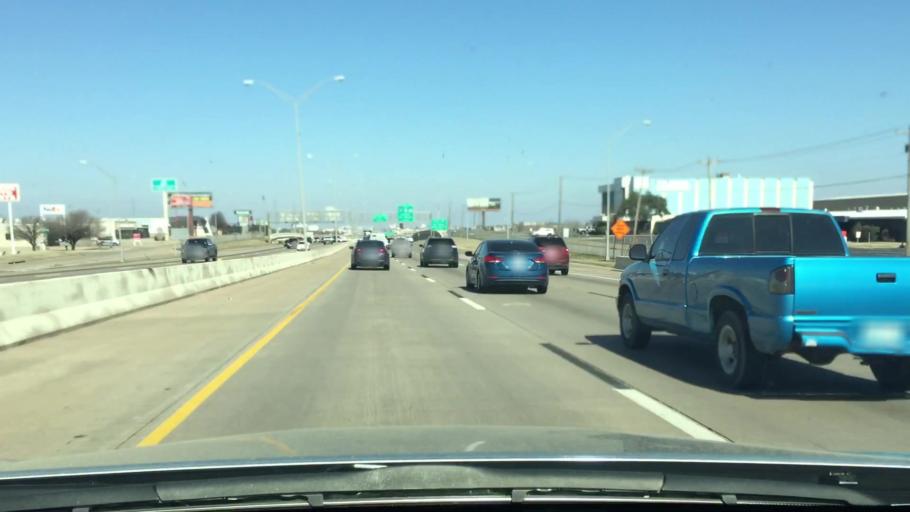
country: US
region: Oklahoma
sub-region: Cleveland County
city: Moore
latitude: 35.3789
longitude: -97.4950
